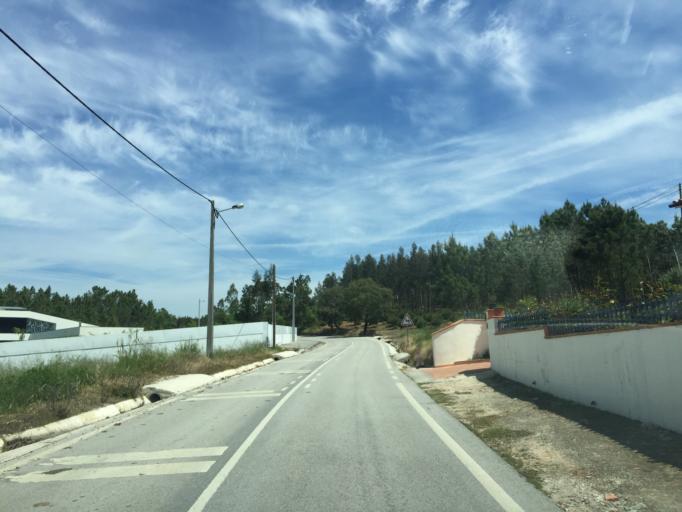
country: PT
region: Coimbra
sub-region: Soure
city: Soure
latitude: 40.0537
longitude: -8.6667
